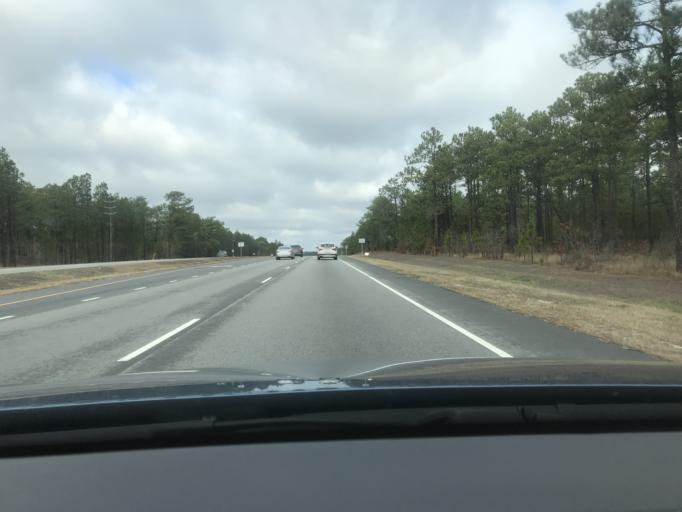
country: US
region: North Carolina
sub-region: Cumberland County
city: Spring Lake
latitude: 35.2187
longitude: -79.0024
